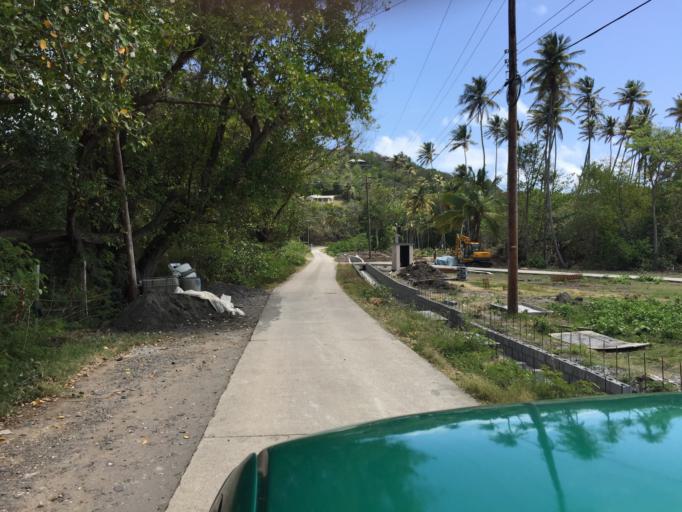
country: VC
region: Grenadines
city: Port Elizabeth
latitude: 13.0204
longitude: -61.2244
